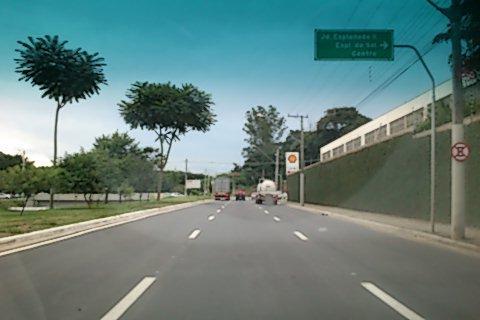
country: BR
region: Sao Paulo
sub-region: Sao Jose Dos Campos
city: Sao Jose dos Campos
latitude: -23.1994
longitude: -45.9117
